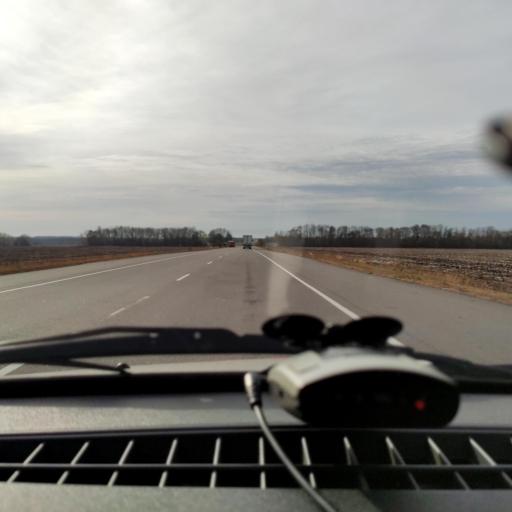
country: RU
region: Voronezj
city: Strelitsa
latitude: 51.5030
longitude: 38.9654
